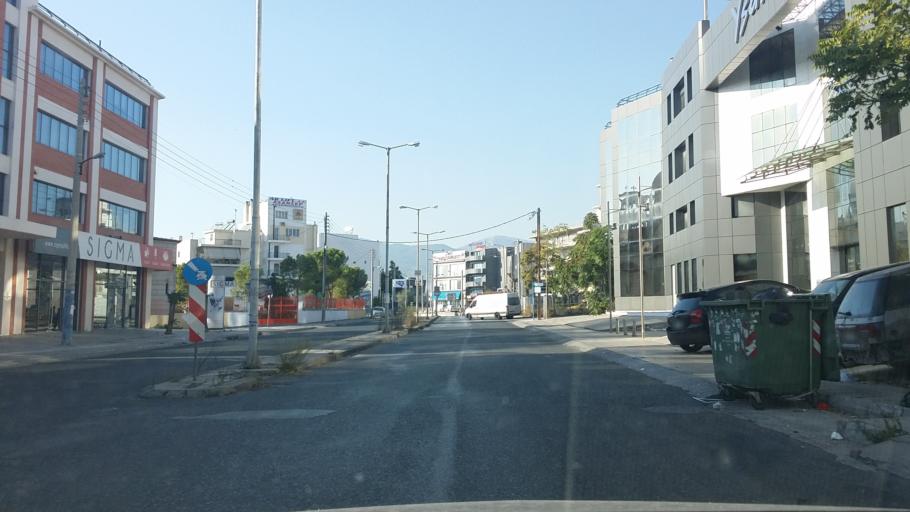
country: GR
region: Attica
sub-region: Nomarchia Athinas
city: Irakleio
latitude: 38.0534
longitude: 23.7475
